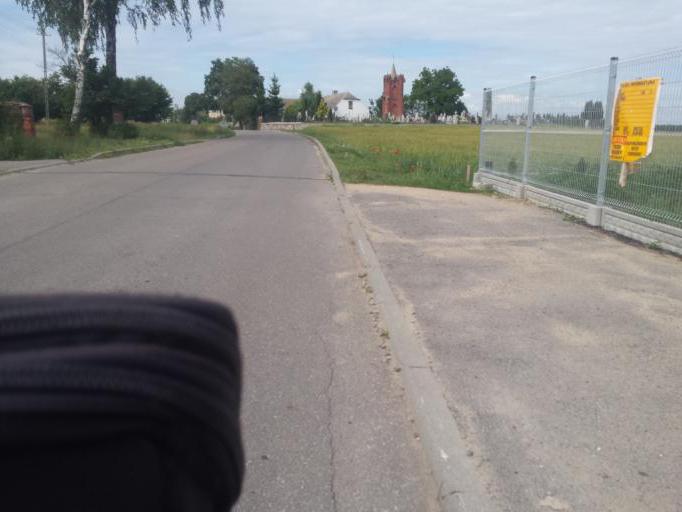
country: PL
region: Warmian-Masurian Voivodeship
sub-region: Powiat nowomiejski
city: Biskupiec
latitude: 53.5379
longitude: 19.4608
